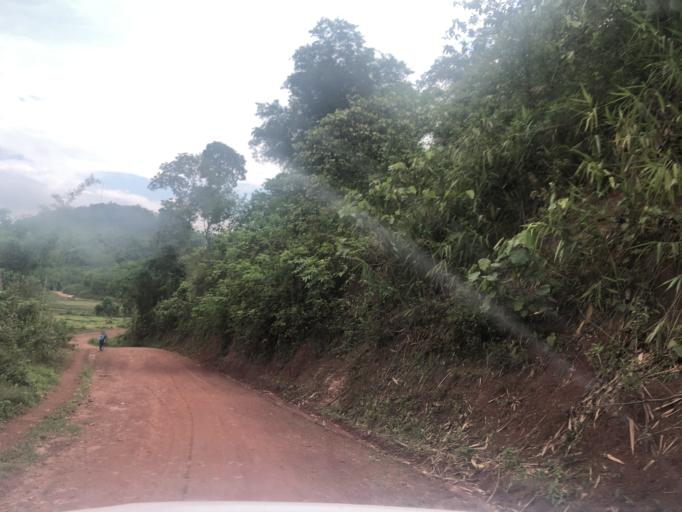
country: LA
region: Oudomxai
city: Muang La
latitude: 21.2356
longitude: 101.9954
